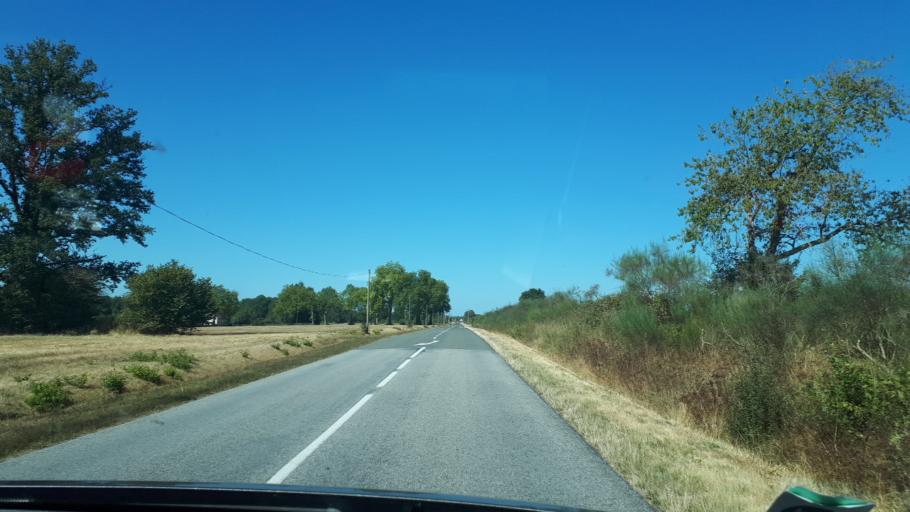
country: FR
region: Centre
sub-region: Departement du Loiret
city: Coullons
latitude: 47.6378
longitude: 2.4416
